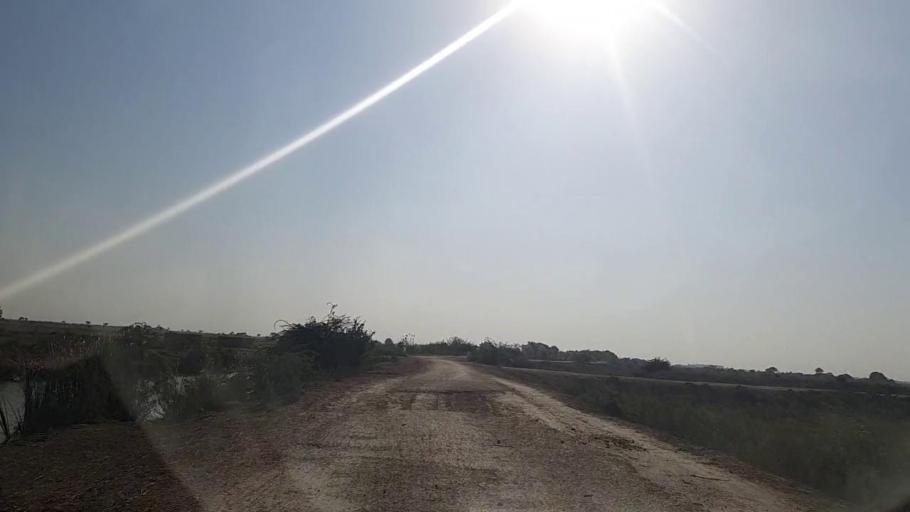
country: PK
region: Sindh
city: Mirpur Batoro
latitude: 24.5529
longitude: 68.1669
